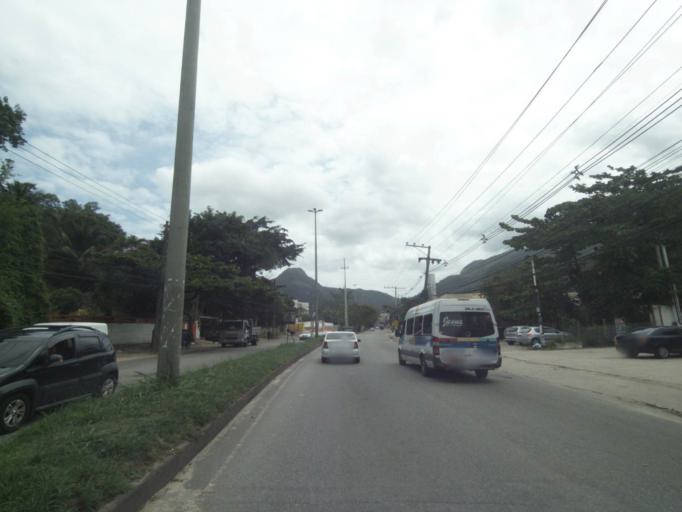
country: BR
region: Rio de Janeiro
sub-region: Nilopolis
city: Nilopolis
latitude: -22.9651
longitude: -43.4073
